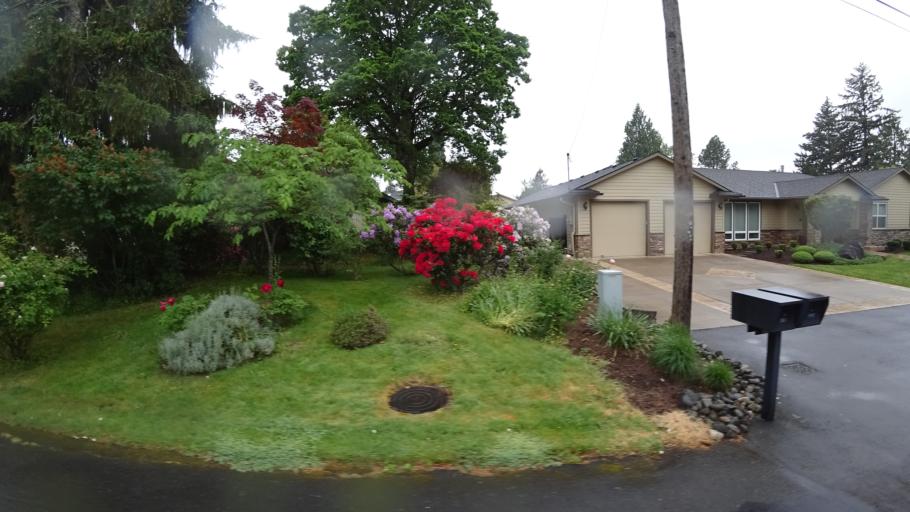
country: US
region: Oregon
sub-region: Washington County
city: Raleigh Hills
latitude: 45.4806
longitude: -122.7711
